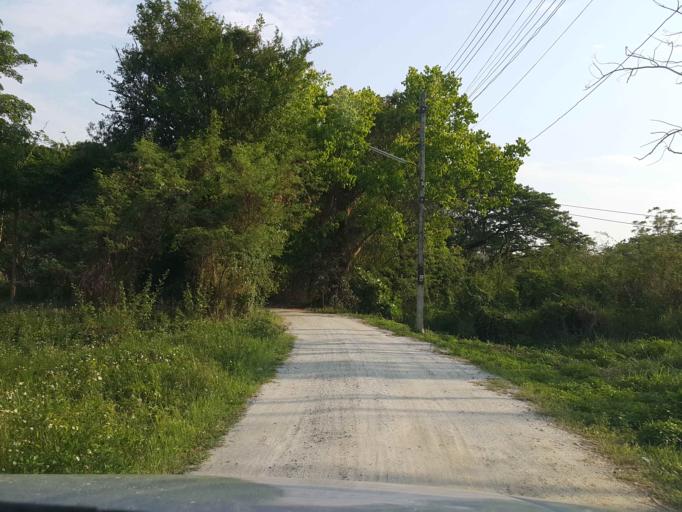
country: TH
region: Chiang Mai
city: Hang Dong
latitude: 18.6907
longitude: 98.9398
